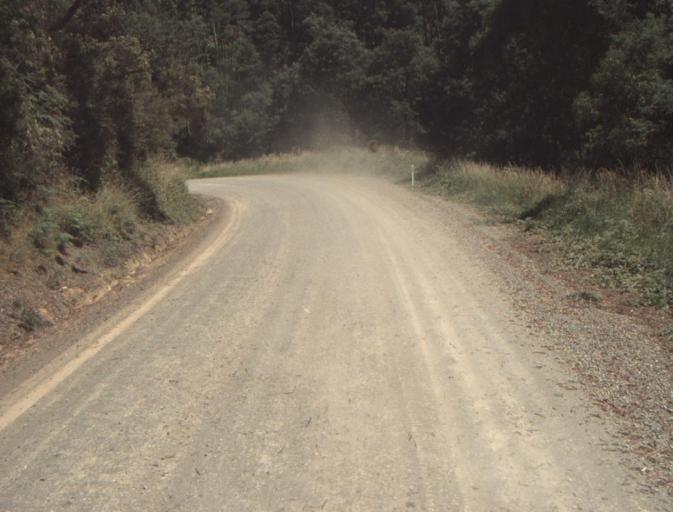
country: AU
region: Tasmania
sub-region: Dorset
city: Scottsdale
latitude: -41.3316
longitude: 147.4297
